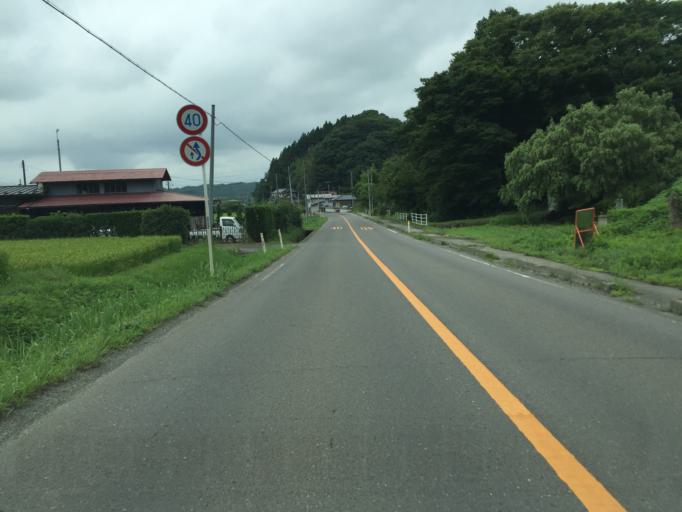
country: JP
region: Miyagi
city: Watari
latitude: 38.0237
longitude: 140.8229
